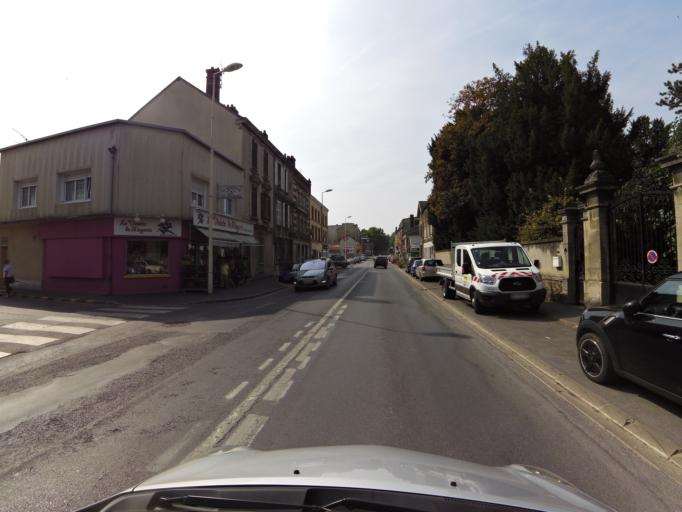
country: FR
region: Champagne-Ardenne
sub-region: Departement de la Marne
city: Magenta
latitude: 49.0486
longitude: 3.9650
